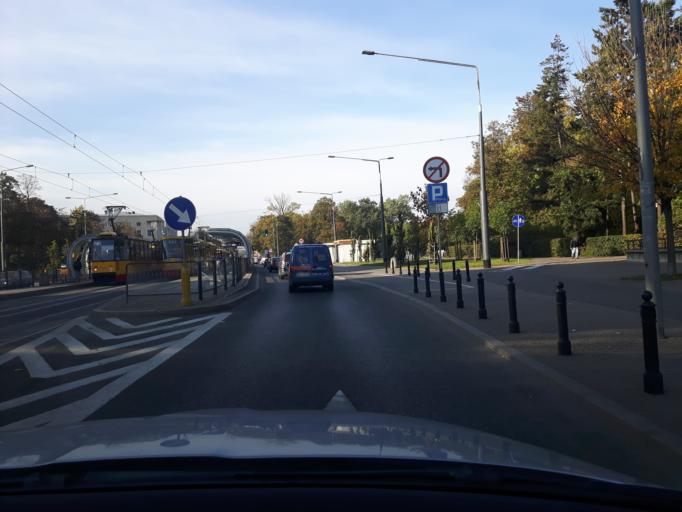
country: PL
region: Masovian Voivodeship
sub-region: Warszawa
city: Praga Polnoc
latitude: 52.2530
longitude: 21.0305
